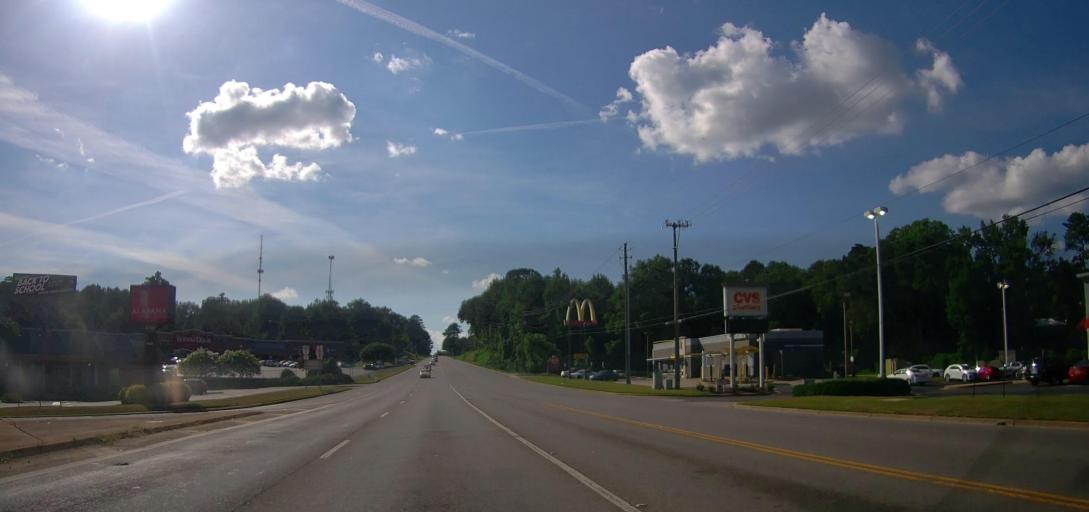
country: US
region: Alabama
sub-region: Tuscaloosa County
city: Holt
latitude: 33.1972
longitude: -87.4792
